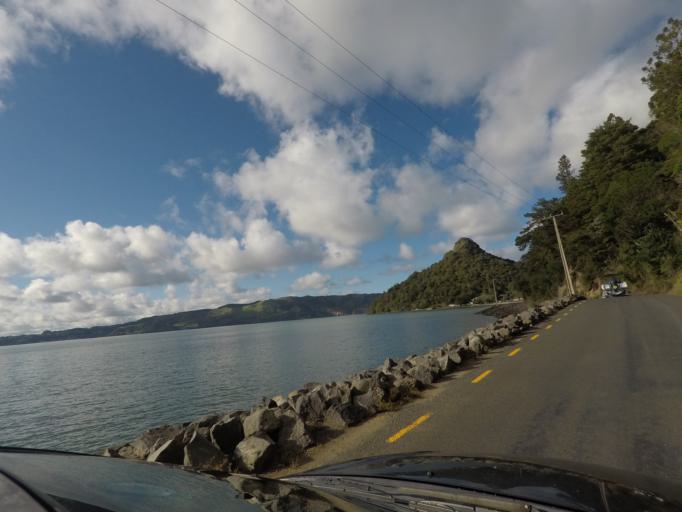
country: NZ
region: Auckland
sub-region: Auckland
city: Titirangi
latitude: -37.0123
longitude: 174.5612
